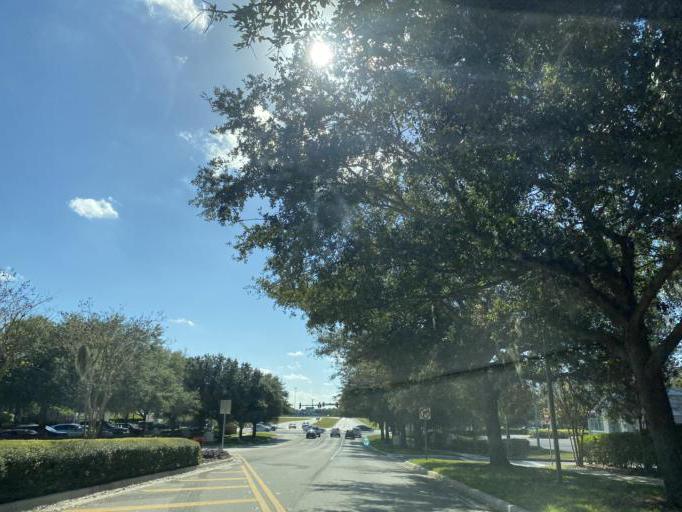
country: US
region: Florida
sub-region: Seminole County
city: Heathrow
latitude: 28.7877
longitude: -81.3543
